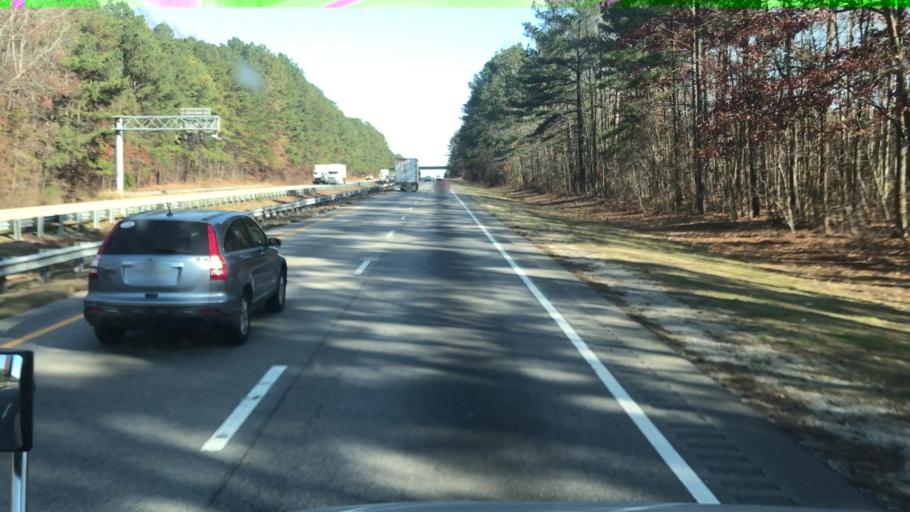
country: US
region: North Carolina
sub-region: Wake County
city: Wendell
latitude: 35.8142
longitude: -78.4049
